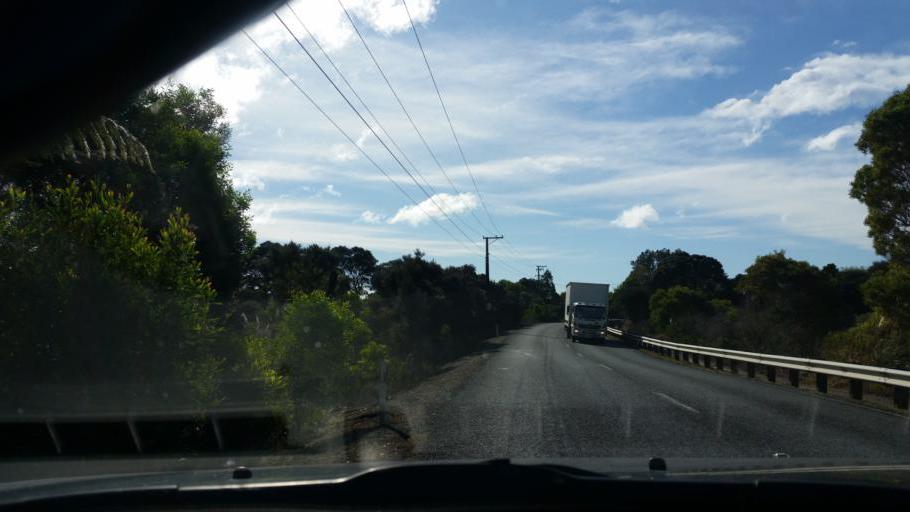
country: NZ
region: Auckland
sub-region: Auckland
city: Wellsford
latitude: -36.1187
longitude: 174.5731
